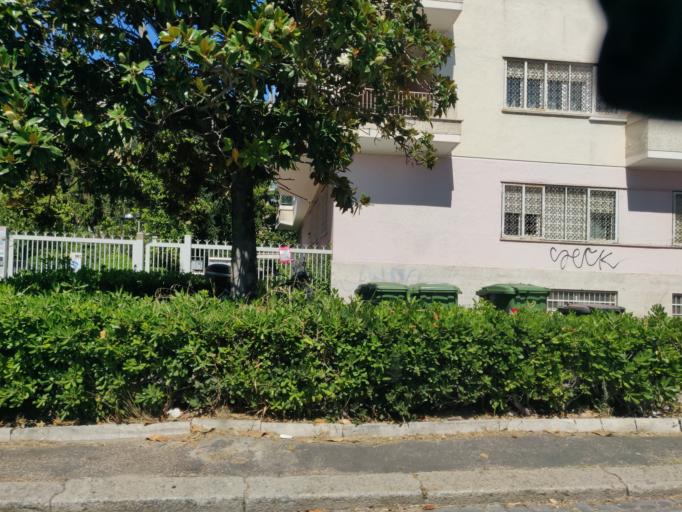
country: IT
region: Latium
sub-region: Citta metropolitana di Roma Capitale
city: Selcetta
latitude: 41.8299
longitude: 12.4744
